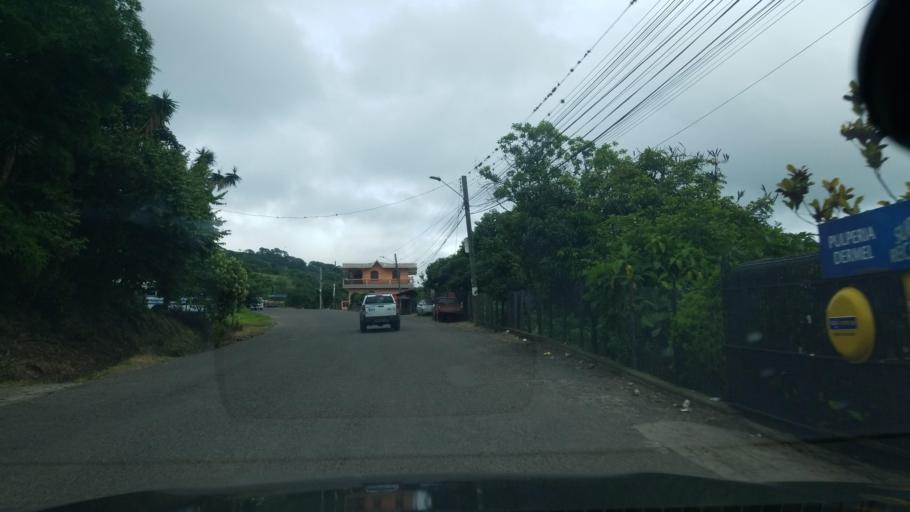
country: HN
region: Choluteca
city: San Marcos de Colon
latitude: 13.4330
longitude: -86.8133
